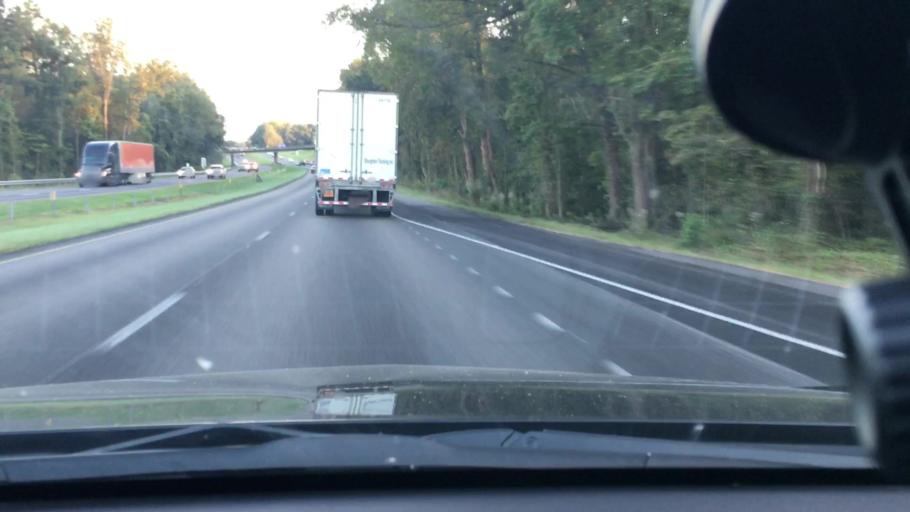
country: US
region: South Carolina
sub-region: Spartanburg County
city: Fairforest
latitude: 34.9641
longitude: -82.0055
